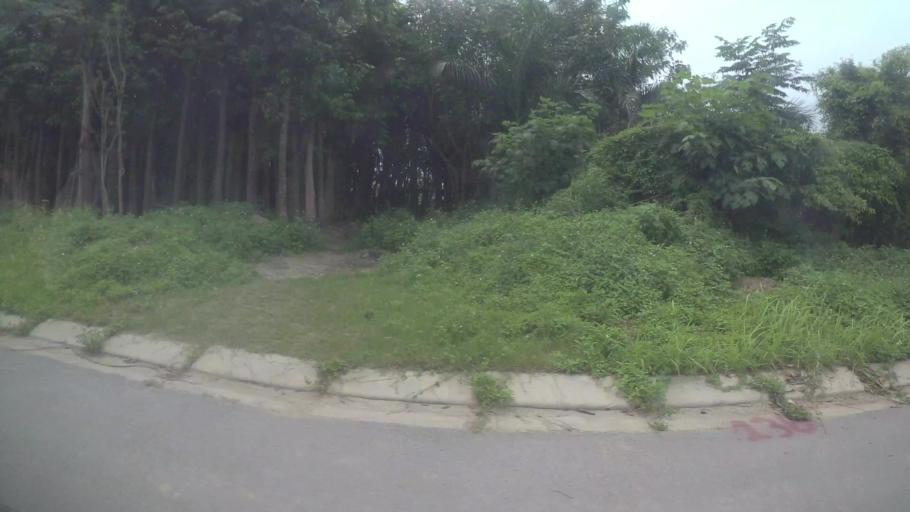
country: VN
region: Ha Noi
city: Cau Dien
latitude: 21.0275
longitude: 105.7418
